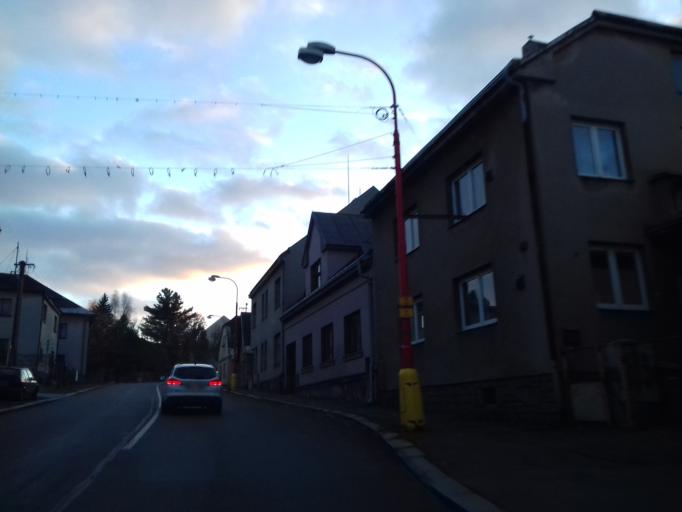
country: CZ
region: Pardubicky
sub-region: Okres Chrudim
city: Hlinsko
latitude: 49.7599
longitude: 15.9053
